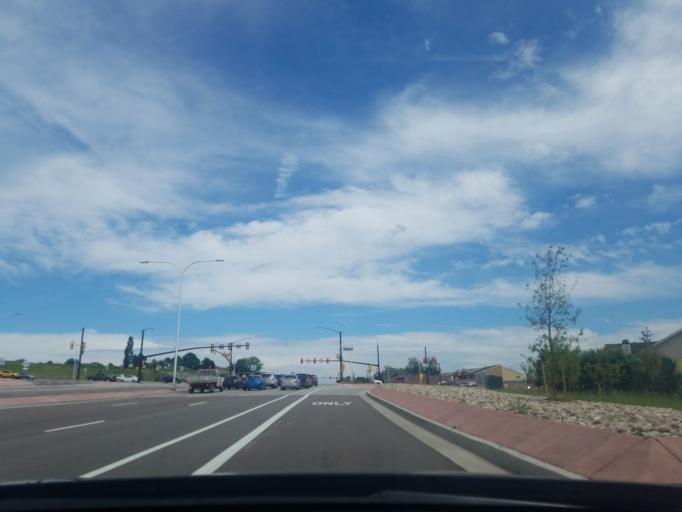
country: US
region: Colorado
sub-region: El Paso County
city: Air Force Academy
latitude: 38.9331
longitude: -104.7766
